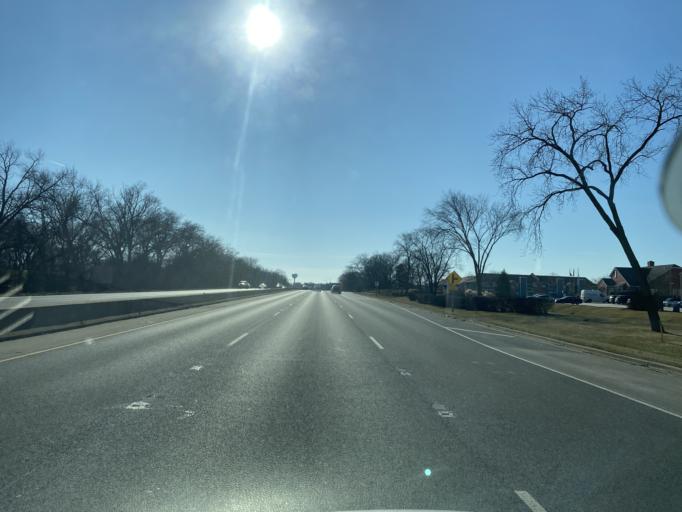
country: US
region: Illinois
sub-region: DuPage County
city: Willowbrook
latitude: 41.7806
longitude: -87.9469
